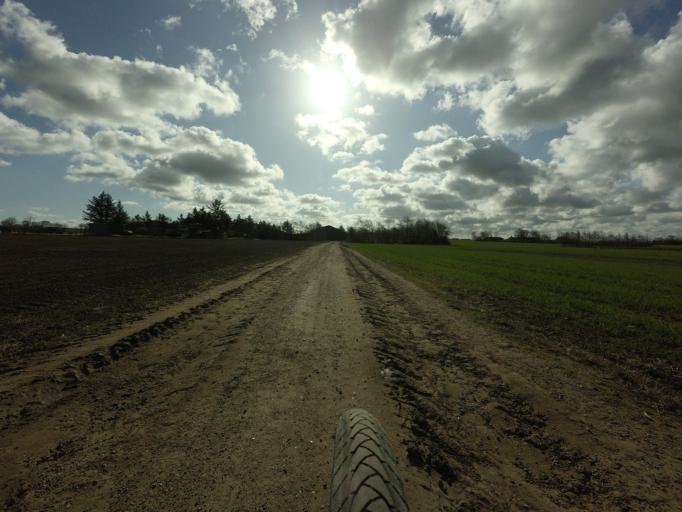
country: DK
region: North Denmark
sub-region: Hjorring Kommune
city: Vra
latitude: 57.3453
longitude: 9.9379
